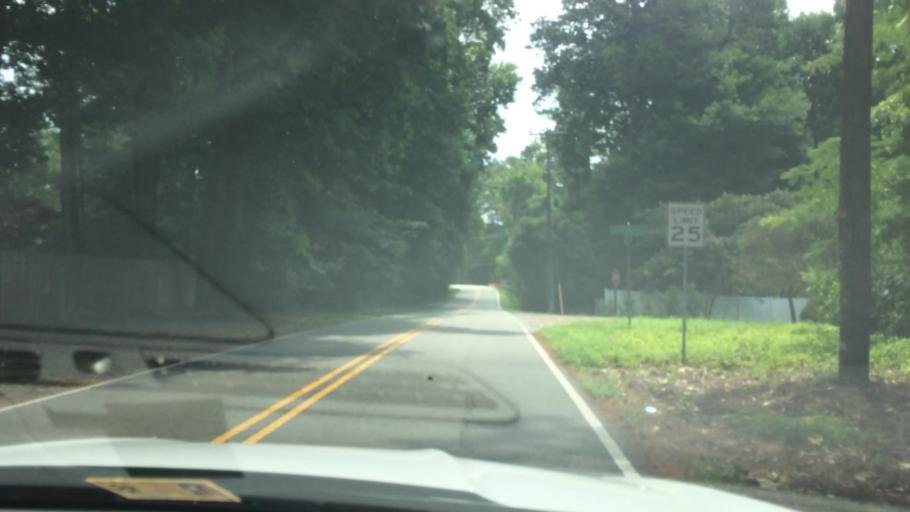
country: US
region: Virginia
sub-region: City of Poquoson
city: Poquoson
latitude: 37.1385
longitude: -76.4551
